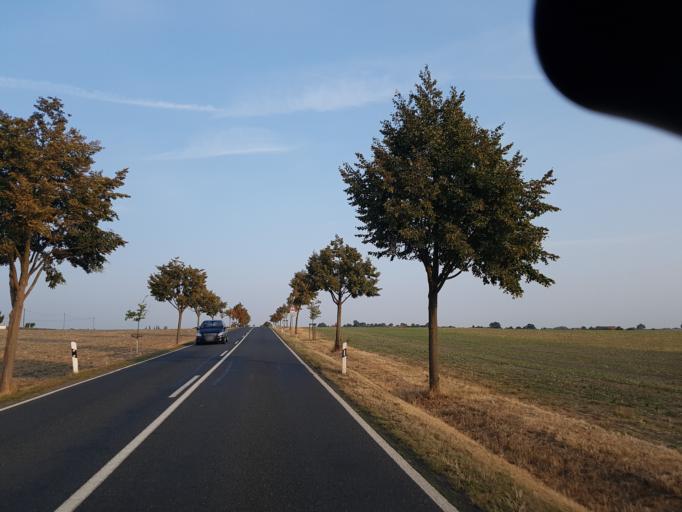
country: DE
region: Saxony
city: Elsnig
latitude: 51.6035
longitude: 12.9376
